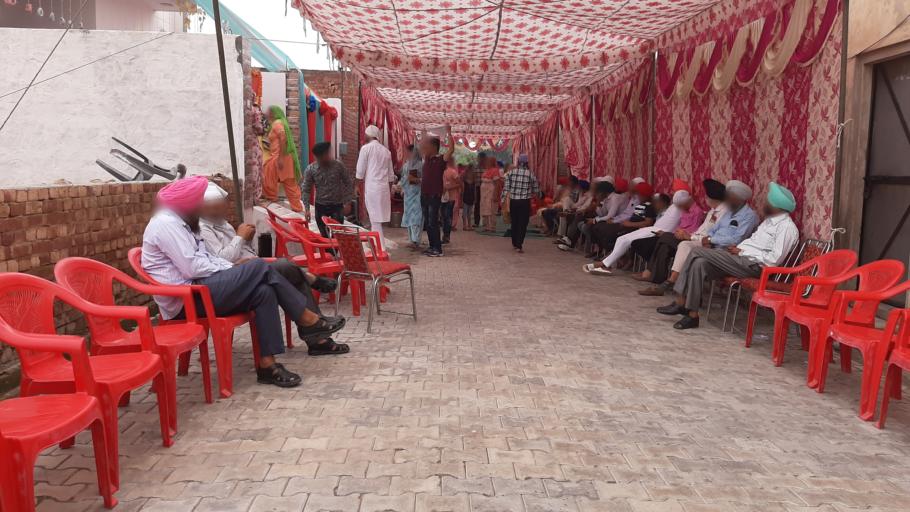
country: IN
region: Punjab
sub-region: Sangrur
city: Sunam
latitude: 30.1359
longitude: 75.8001
